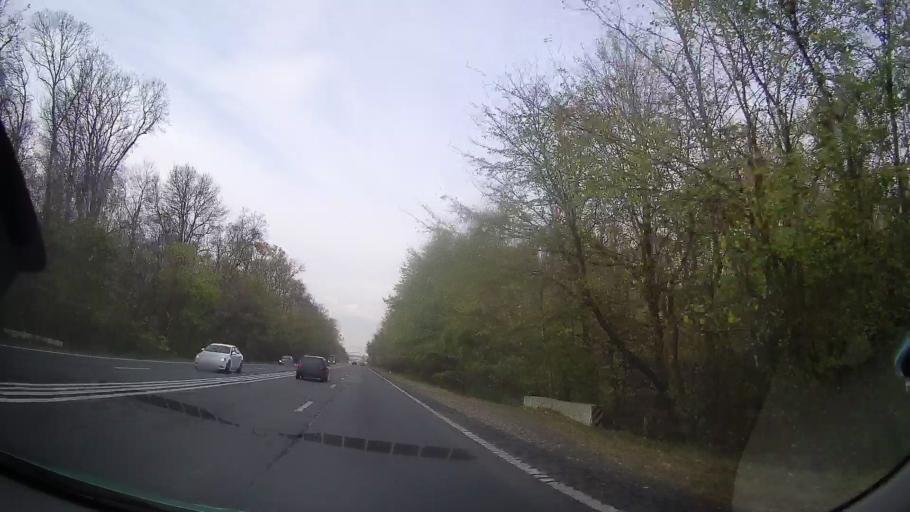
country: RO
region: Prahova
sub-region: Comuna Puchenii Mari
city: Pietrosani
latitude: 44.8434
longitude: 26.0783
